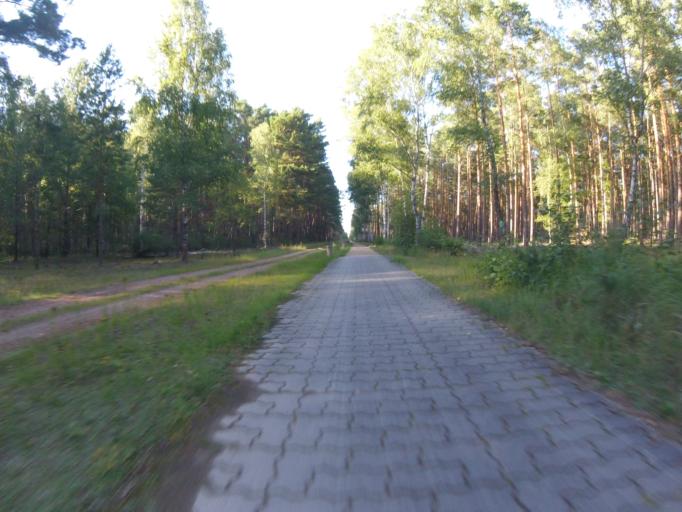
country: DE
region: Brandenburg
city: Halbe
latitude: 52.1842
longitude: 13.7580
